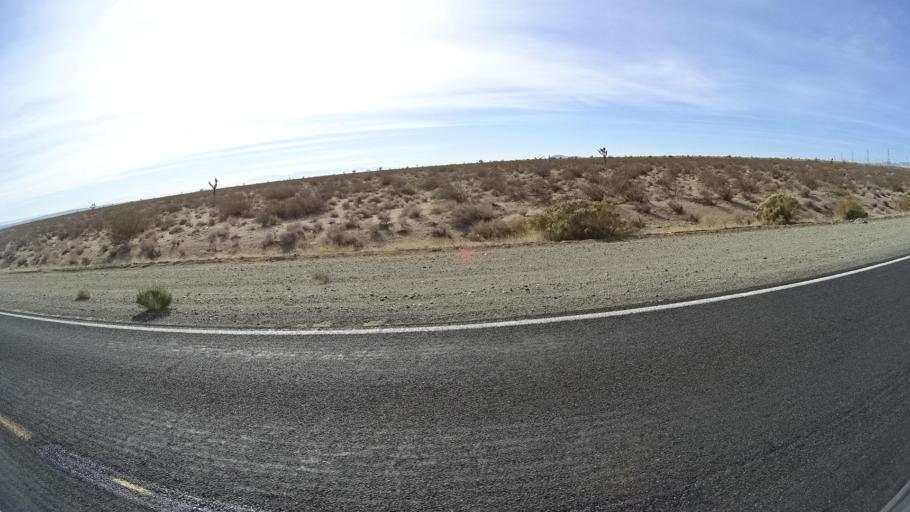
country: US
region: California
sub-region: Kern County
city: Mojave
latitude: 35.1251
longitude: -118.1537
